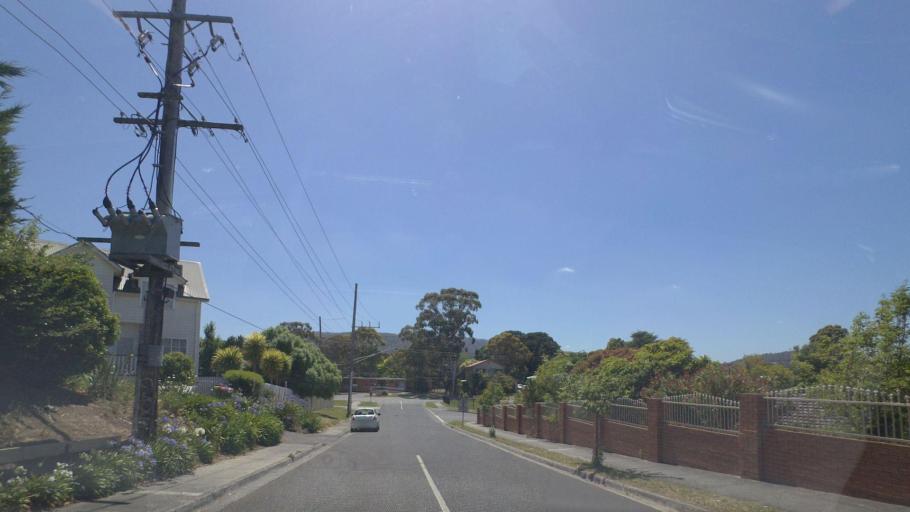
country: AU
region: Victoria
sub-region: Knox
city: Ferntree Gully
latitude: -37.8959
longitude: 145.2876
